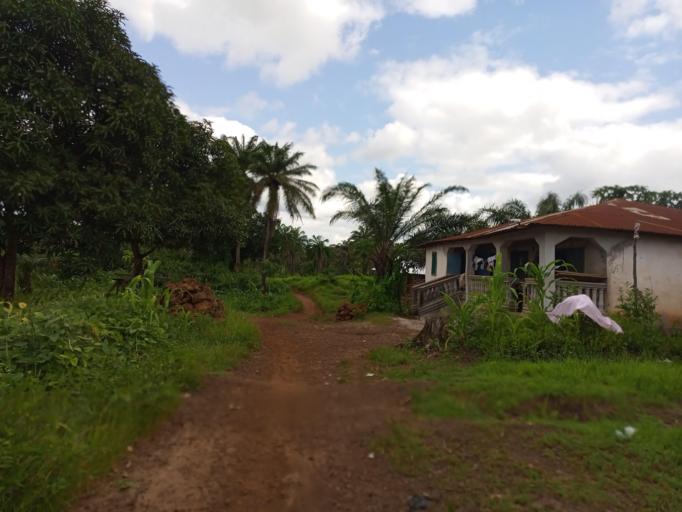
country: SL
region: Northern Province
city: Kamakwie
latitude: 9.4958
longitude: -12.2336
